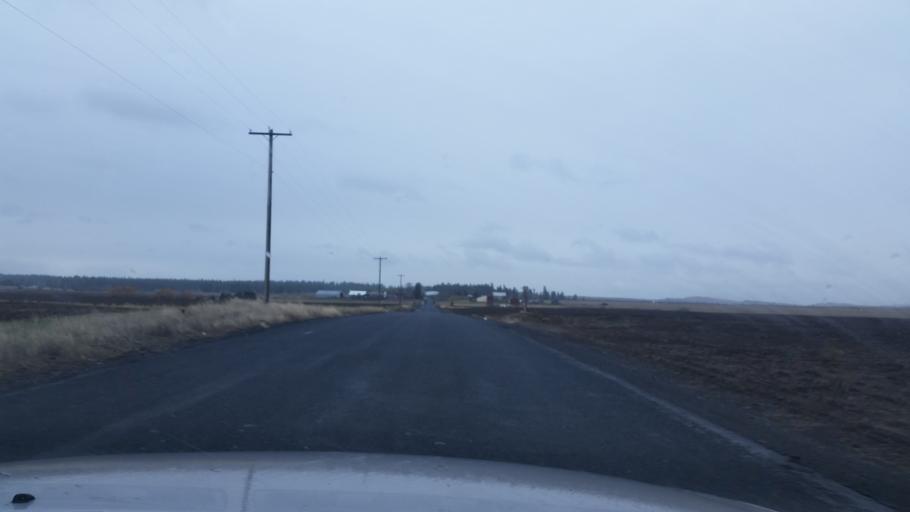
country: US
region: Washington
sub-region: Spokane County
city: Medical Lake
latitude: 47.6144
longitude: -117.7568
